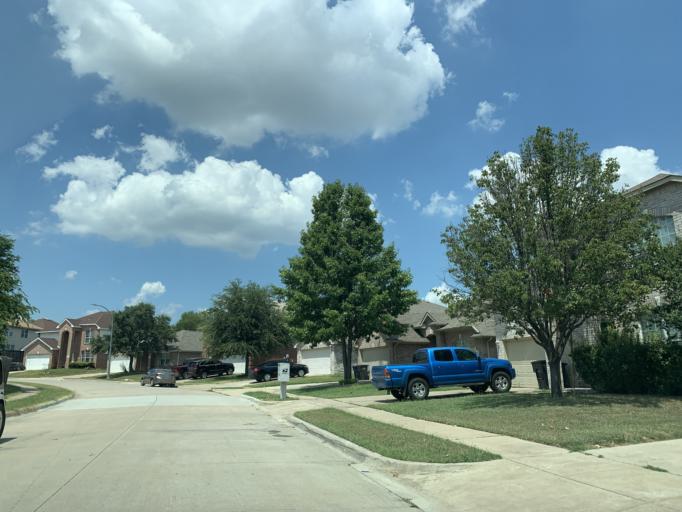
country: US
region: Texas
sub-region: Tarrant County
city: White Settlement
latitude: 32.7265
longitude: -97.5000
